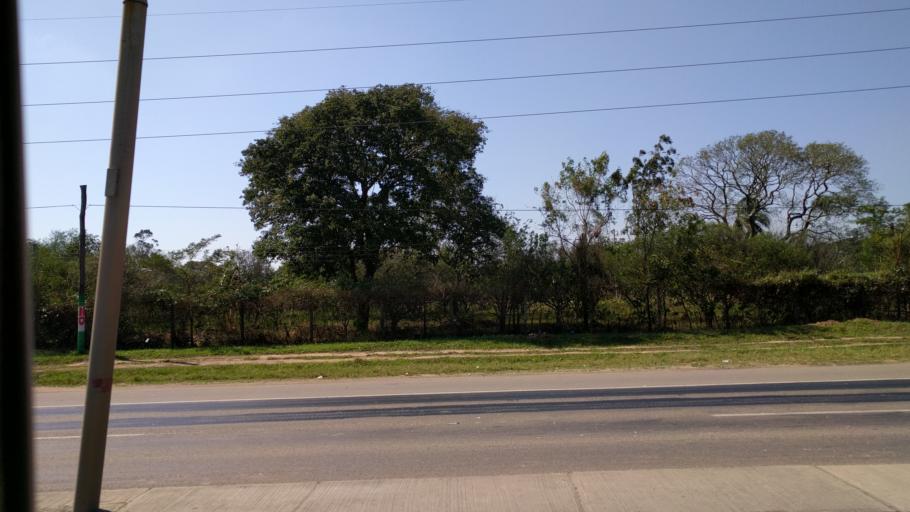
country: BO
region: Santa Cruz
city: Cotoca
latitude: -17.7648
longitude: -63.0615
